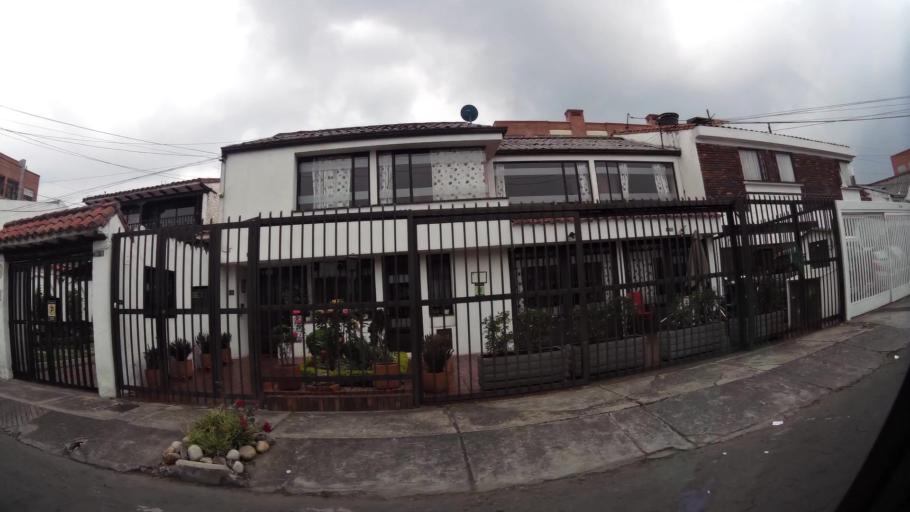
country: CO
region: Bogota D.C.
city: Barrio San Luis
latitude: 4.7158
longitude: -74.0355
